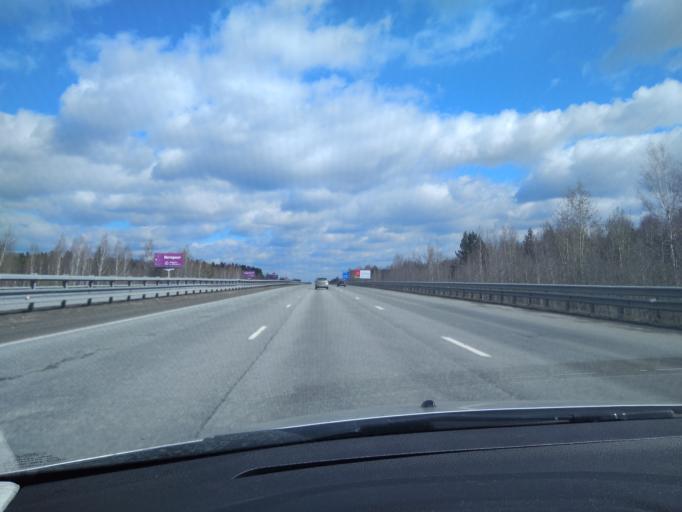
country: RU
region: Sverdlovsk
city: Shuvakish
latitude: 56.9249
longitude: 60.5093
